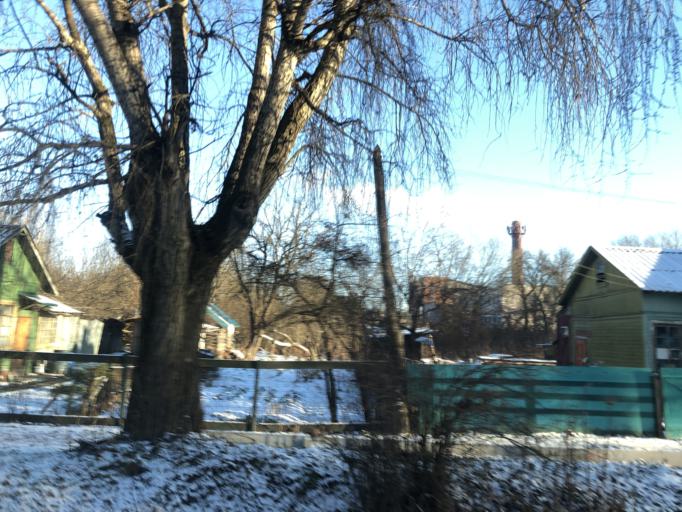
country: RU
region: Tverskaya
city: Rzhev
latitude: 56.2734
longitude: 34.3221
